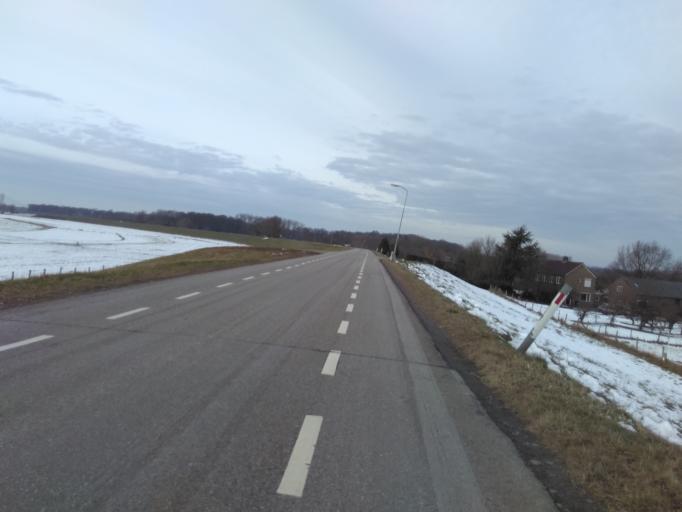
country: NL
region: Gelderland
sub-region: Gemeente Beuningen
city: Beuningen
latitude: 51.8846
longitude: 5.7791
